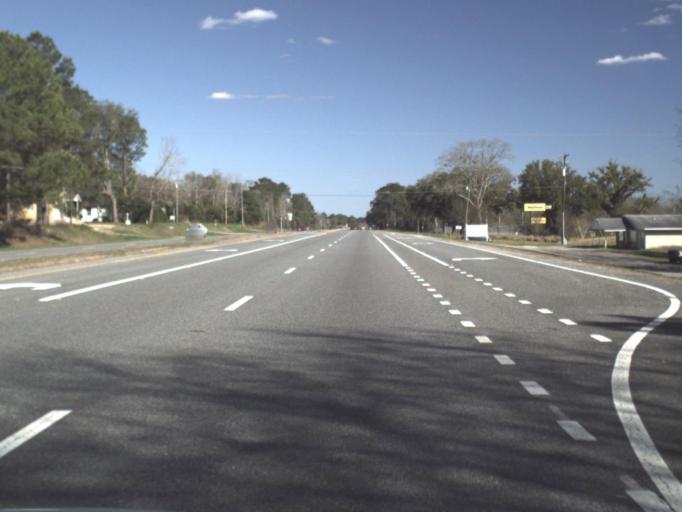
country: US
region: Florida
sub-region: Gadsden County
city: Midway
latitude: 30.4973
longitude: -84.4411
